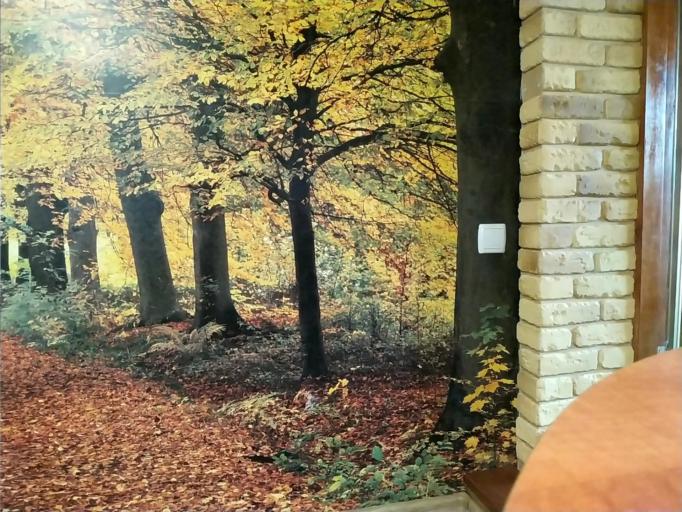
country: RU
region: Leningrad
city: Tolmachevo
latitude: 58.9308
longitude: 29.7167
